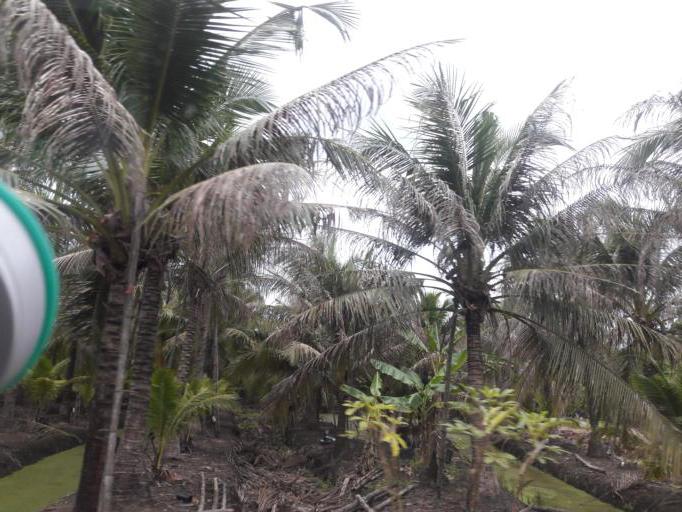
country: TH
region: Ratchaburi
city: Damnoen Saduak
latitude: 13.5086
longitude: 100.0146
